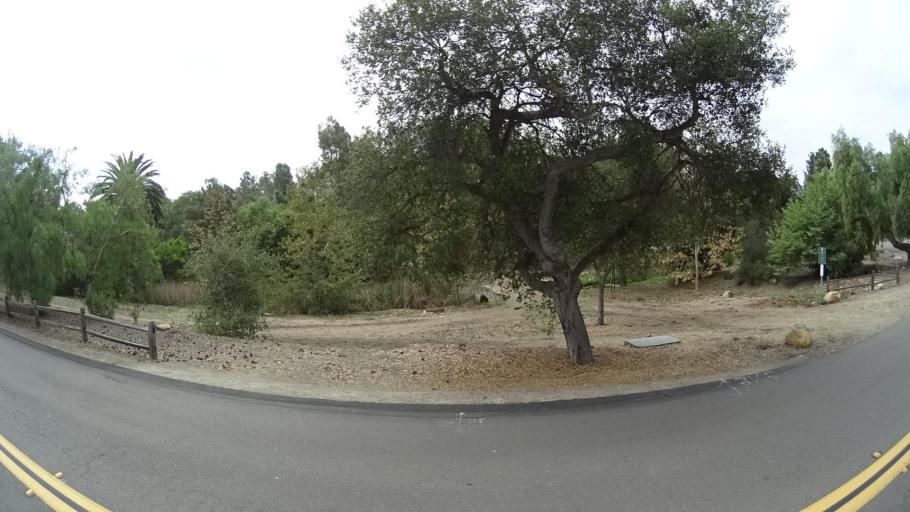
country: US
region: California
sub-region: San Diego County
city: Rancho Santa Fe
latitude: 33.0234
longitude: -117.2268
